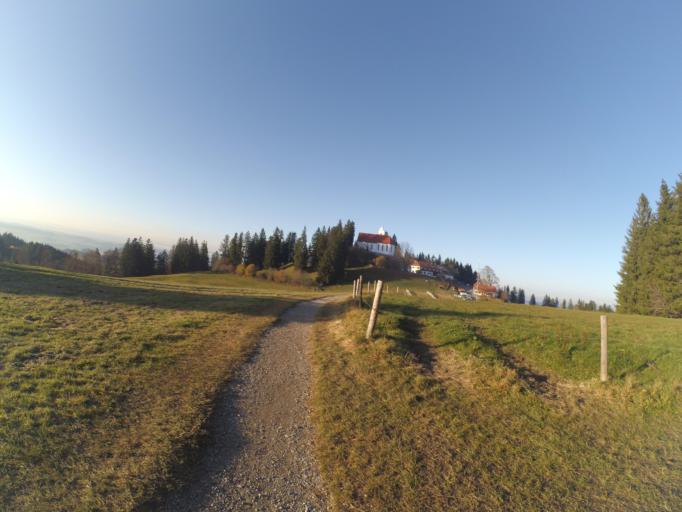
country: DE
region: Bavaria
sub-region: Upper Bavaria
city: Bernbeuren
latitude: 47.7333
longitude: 10.7367
